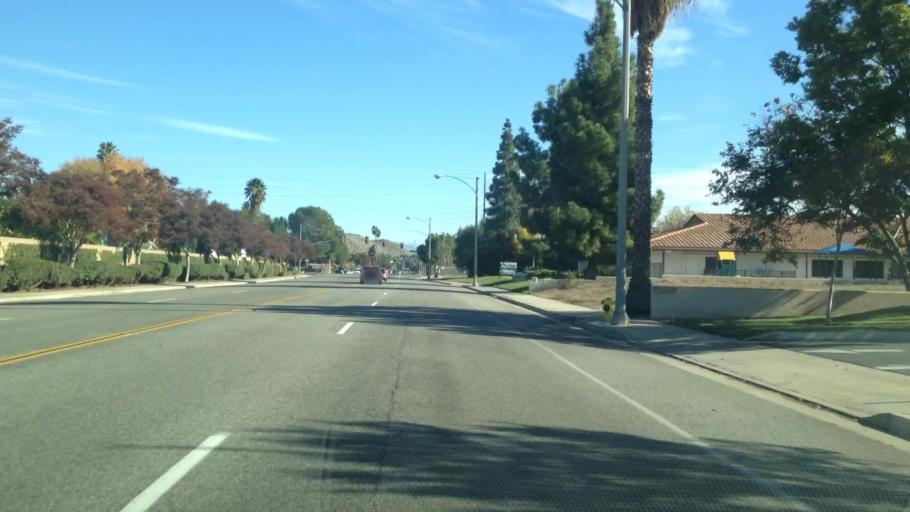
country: US
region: California
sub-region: Riverside County
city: Home Gardens
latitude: 33.9108
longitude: -117.4848
